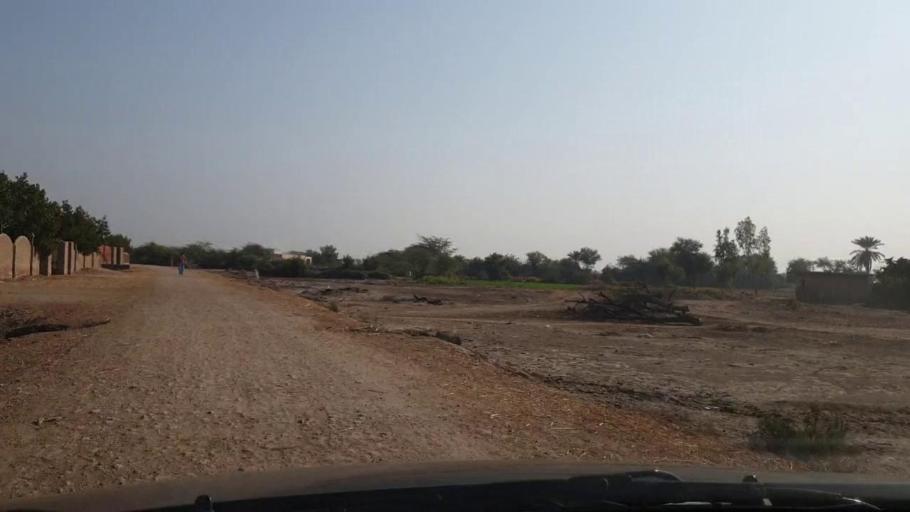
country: PK
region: Sindh
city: Sanghar
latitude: 25.9638
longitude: 69.0123
